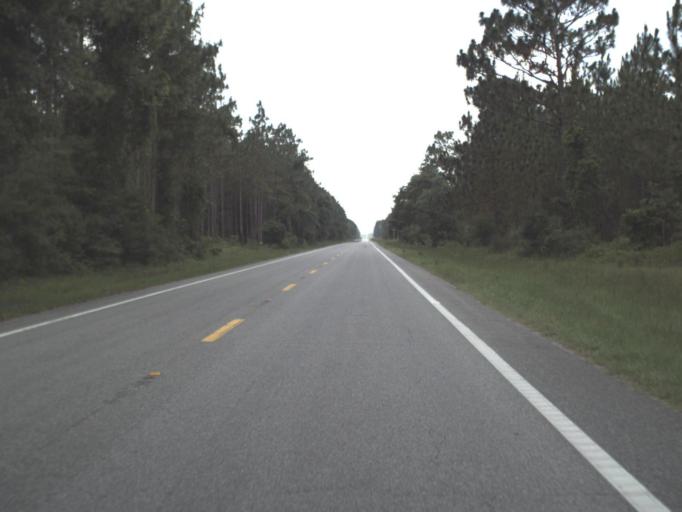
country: US
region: Florida
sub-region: Madison County
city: Madison
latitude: 30.4012
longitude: -83.2136
